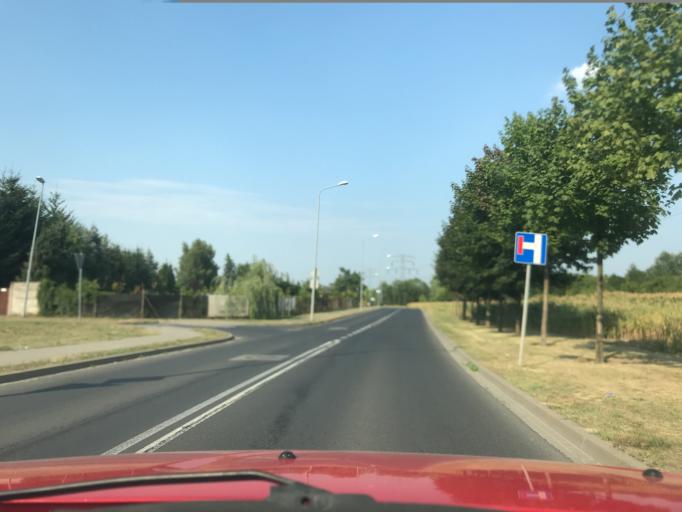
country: PL
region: Greater Poland Voivodeship
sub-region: Powiat poznanski
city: Plewiska
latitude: 52.3629
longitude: 16.8516
